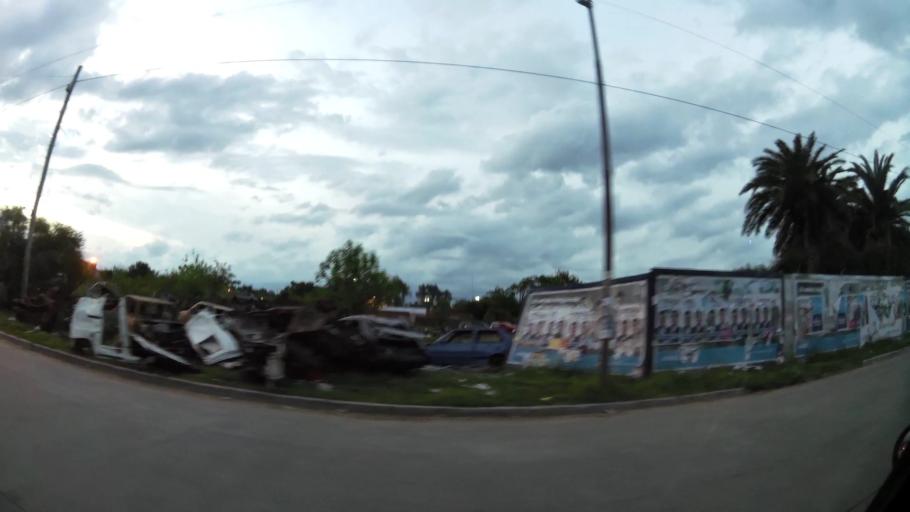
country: AR
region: Buenos Aires
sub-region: Partido de Quilmes
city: Quilmes
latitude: -34.7194
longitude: -58.2348
